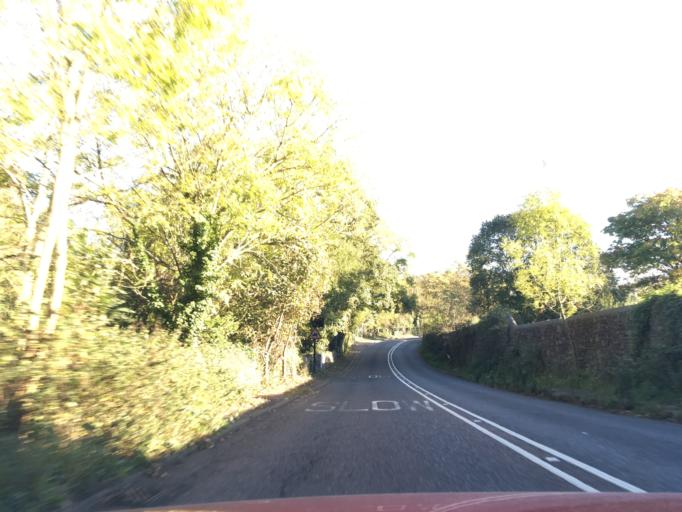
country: GB
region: England
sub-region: Bristol
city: Bristol
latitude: 51.4493
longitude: -2.6271
